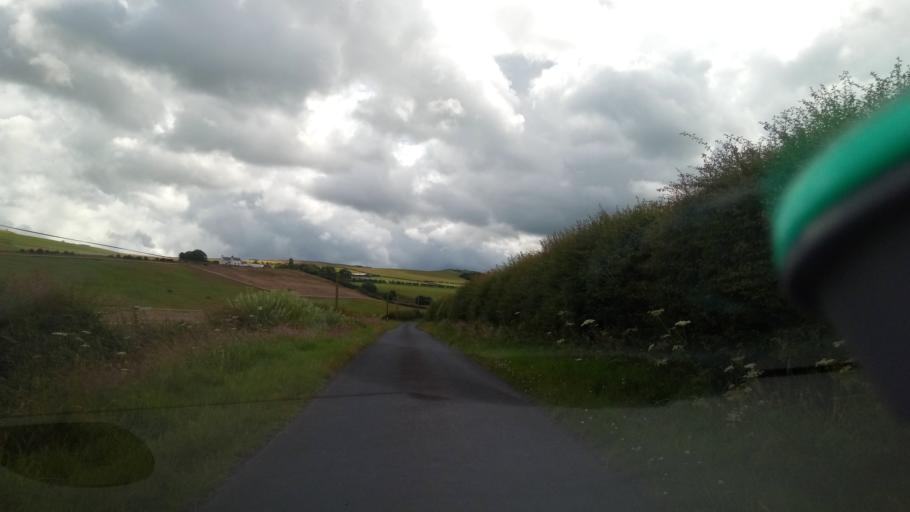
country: GB
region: Scotland
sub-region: The Scottish Borders
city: Kelso
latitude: 55.4934
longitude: -2.4281
